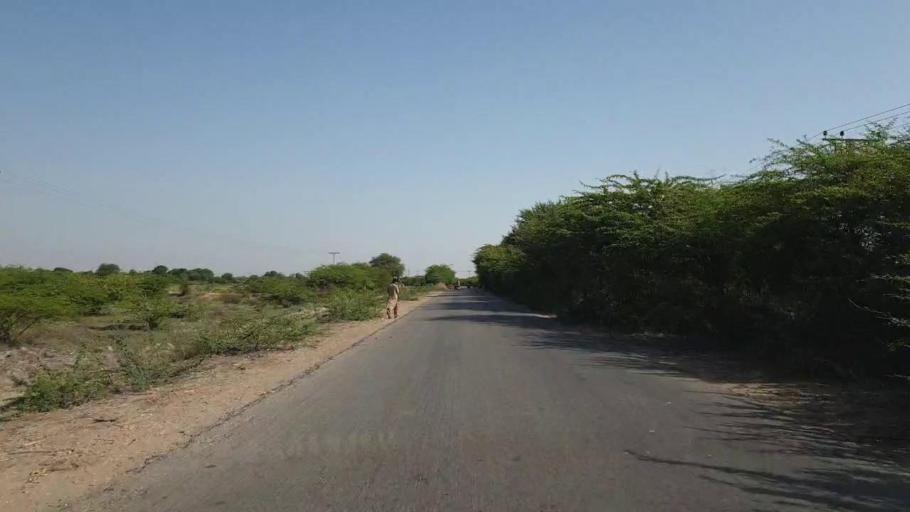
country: PK
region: Sindh
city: Chor
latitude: 25.4845
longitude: 69.7797
